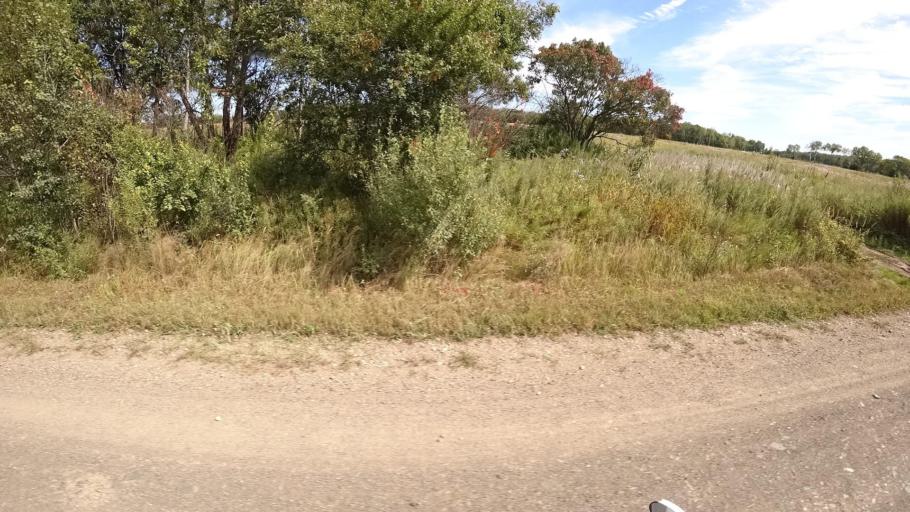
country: RU
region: Primorskiy
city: Yakovlevka
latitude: 44.7179
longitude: 133.6170
